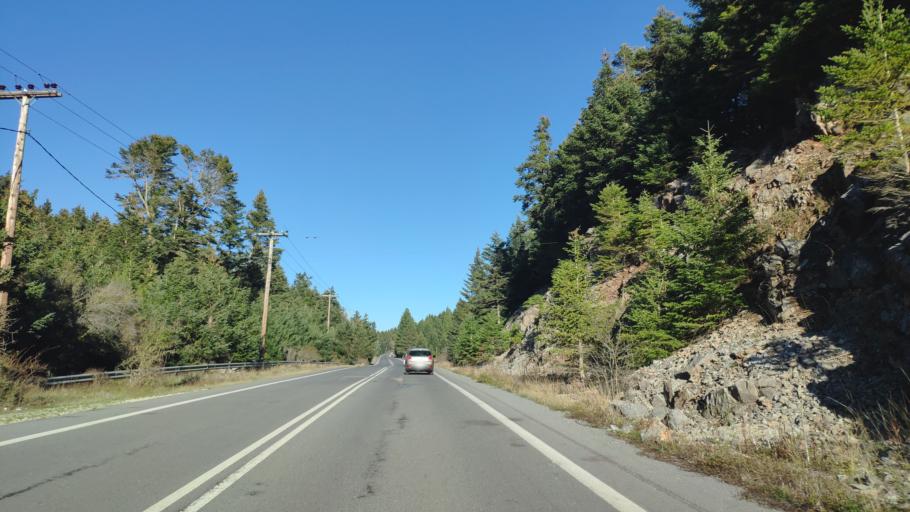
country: GR
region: Peloponnese
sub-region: Nomos Arkadias
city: Dimitsana
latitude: 37.6447
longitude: 22.1083
